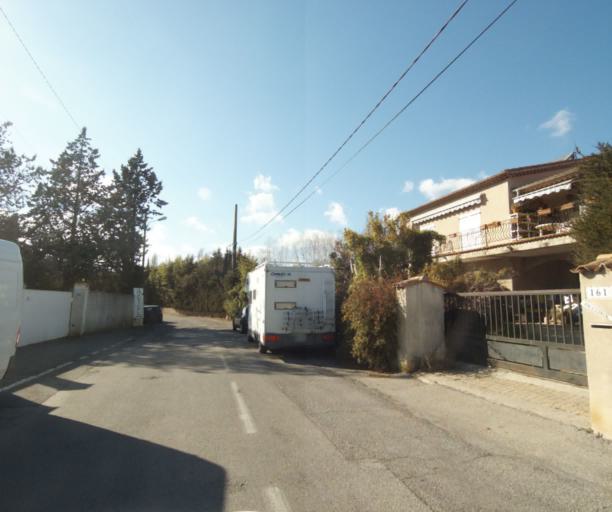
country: FR
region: Provence-Alpes-Cote d'Azur
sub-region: Departement des Alpes-Maritimes
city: Biot
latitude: 43.6146
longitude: 7.1190
